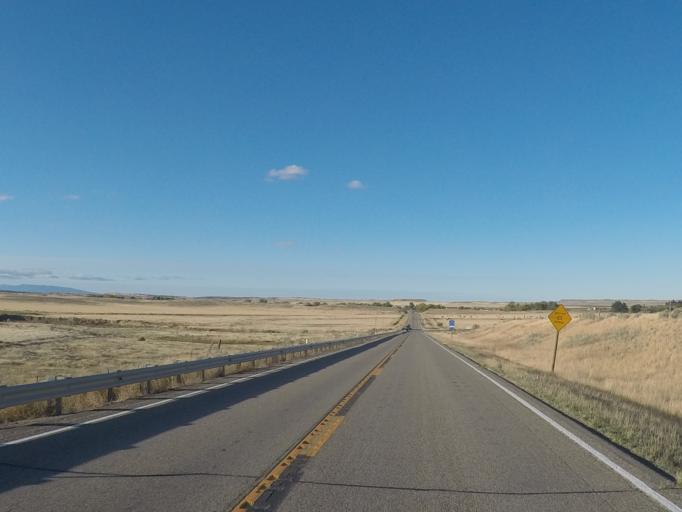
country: US
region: Montana
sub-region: Golden Valley County
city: Ryegate
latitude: 46.2777
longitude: -108.9400
